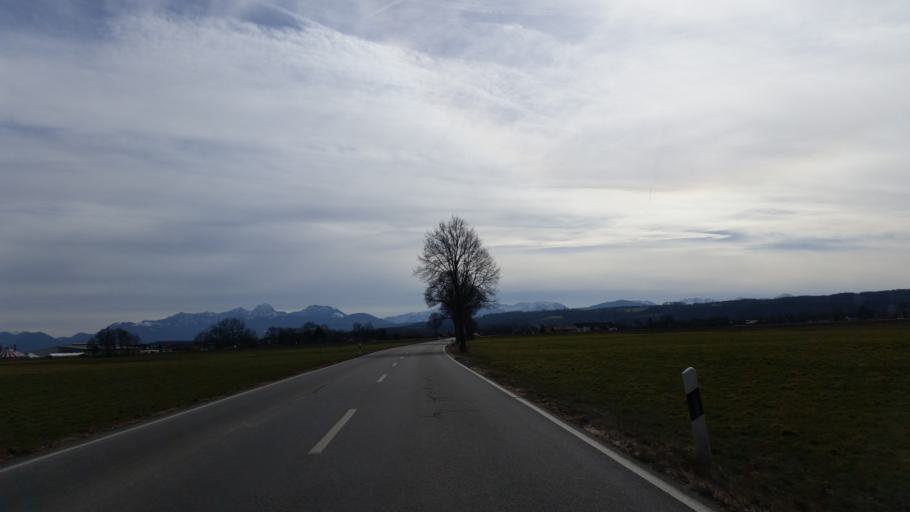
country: DE
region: Bavaria
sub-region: Upper Bavaria
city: Bruckmuhl
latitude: 47.8910
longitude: 11.9273
